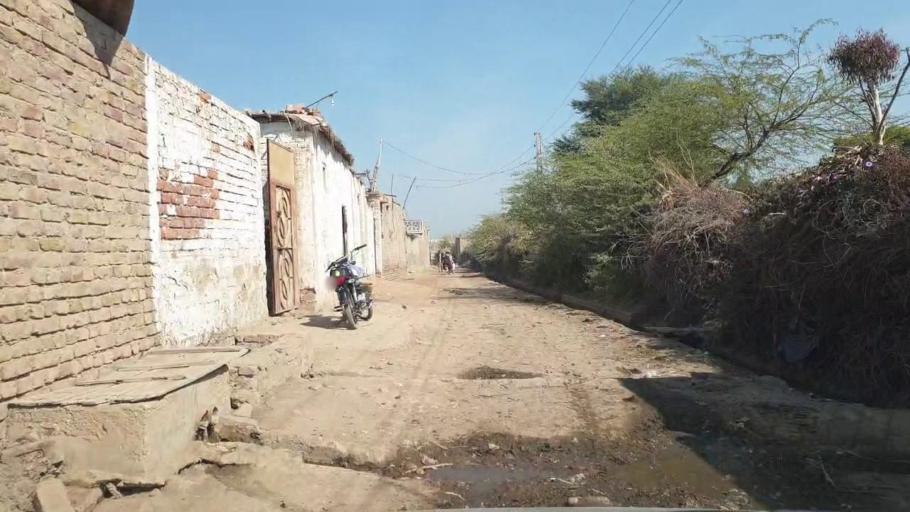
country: PK
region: Sindh
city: Tando Allahyar
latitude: 25.3883
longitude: 68.7825
